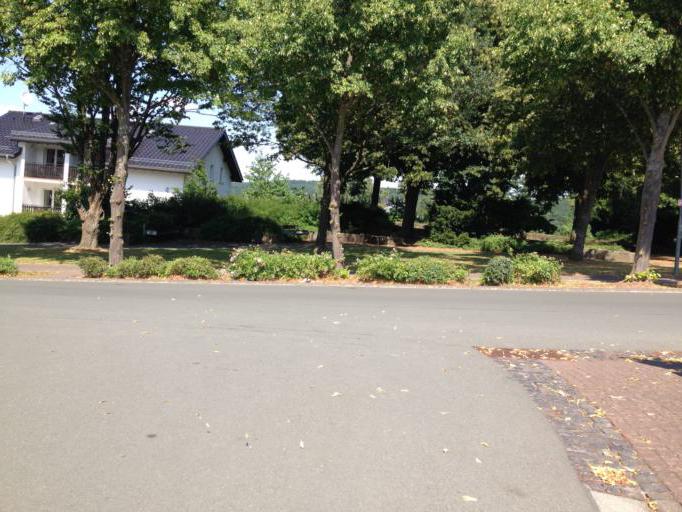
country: DE
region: Hesse
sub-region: Regierungsbezirk Giessen
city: Heuchelheim
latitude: 50.6185
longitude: 8.6354
